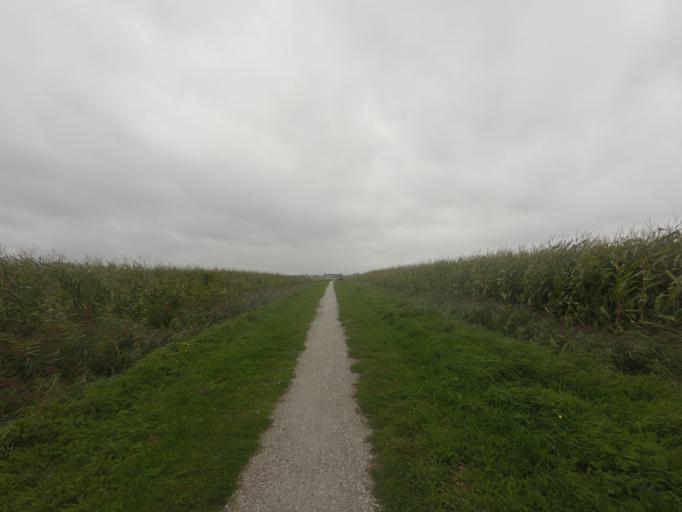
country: NL
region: Friesland
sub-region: Gemeente Ferwerderadiel
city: Ferwert
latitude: 53.3470
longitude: 5.8582
